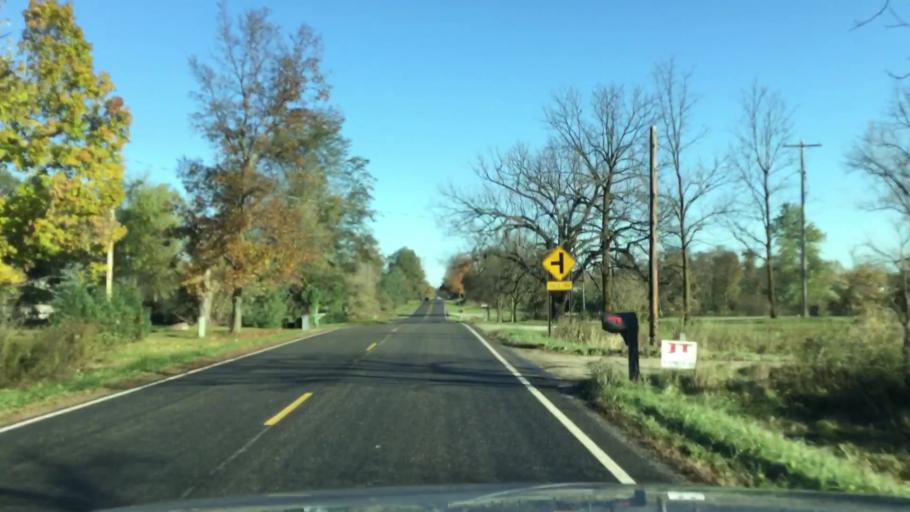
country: US
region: Michigan
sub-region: Shiawassee County
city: Durand
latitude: 42.8518
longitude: -83.9459
